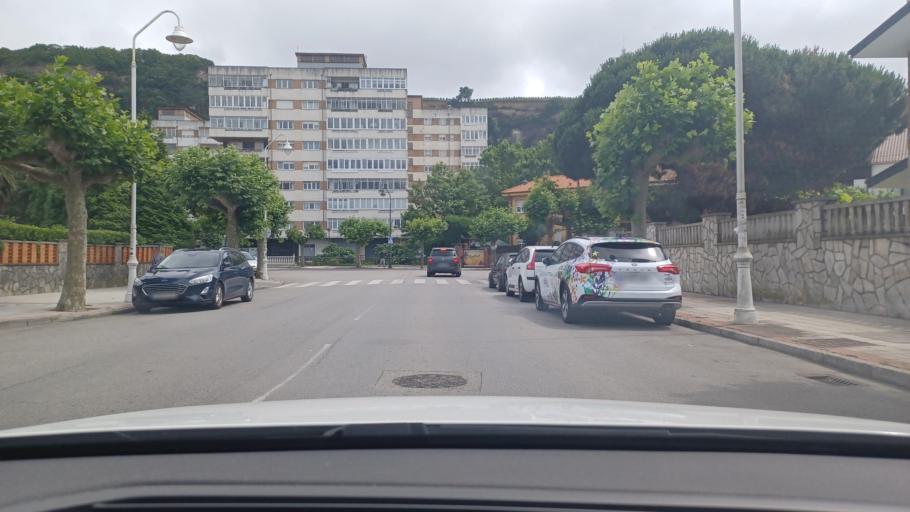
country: ES
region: Asturias
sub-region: Province of Asturias
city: Aviles
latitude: 43.5740
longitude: -5.9537
